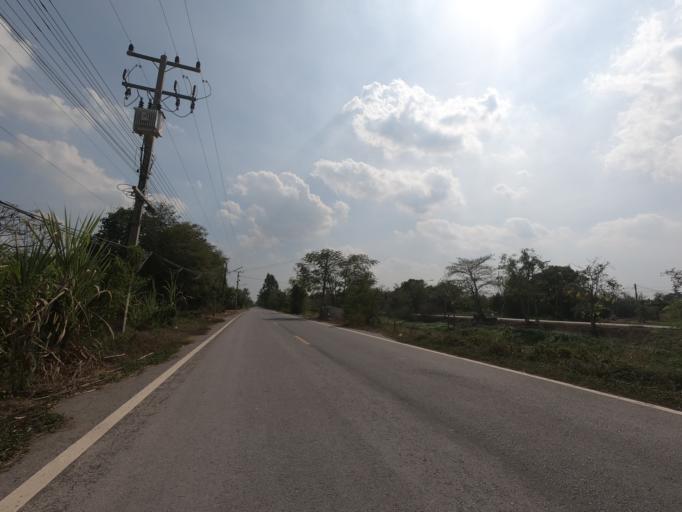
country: TH
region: Pathum Thani
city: Nong Suea
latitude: 14.2050
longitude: 100.8462
